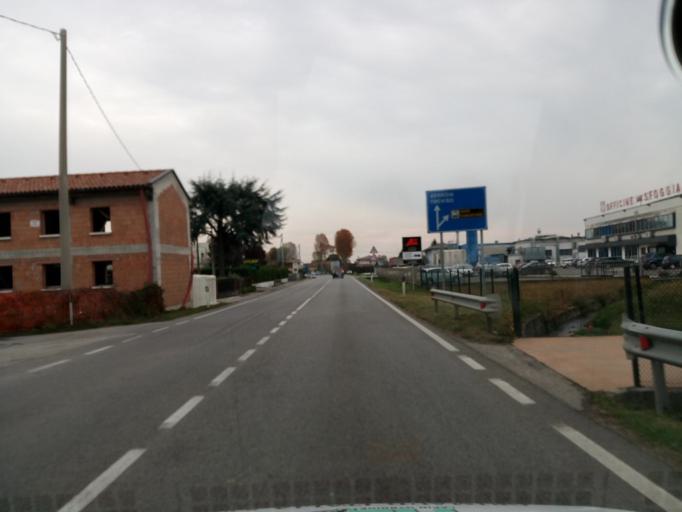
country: IT
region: Veneto
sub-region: Provincia di Treviso
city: Venegazzu
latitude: 45.7673
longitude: 12.0800
